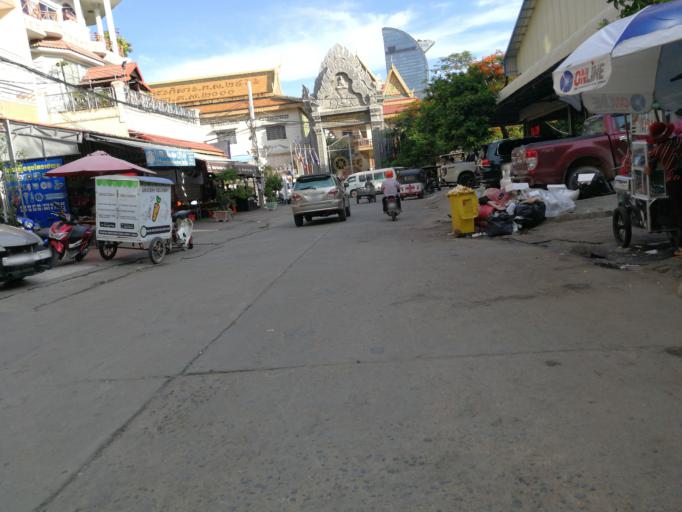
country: KH
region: Phnom Penh
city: Phnom Penh
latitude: 11.5802
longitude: 104.9186
